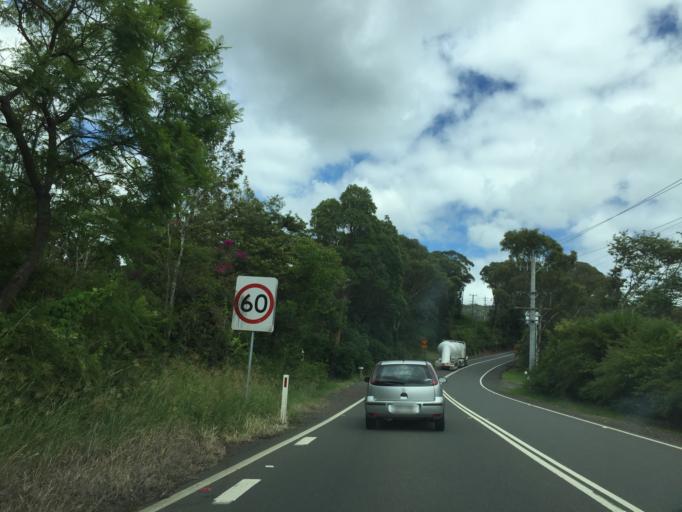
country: AU
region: New South Wales
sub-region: Hawkesbury
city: Richmond
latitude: -33.5476
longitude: 150.6527
